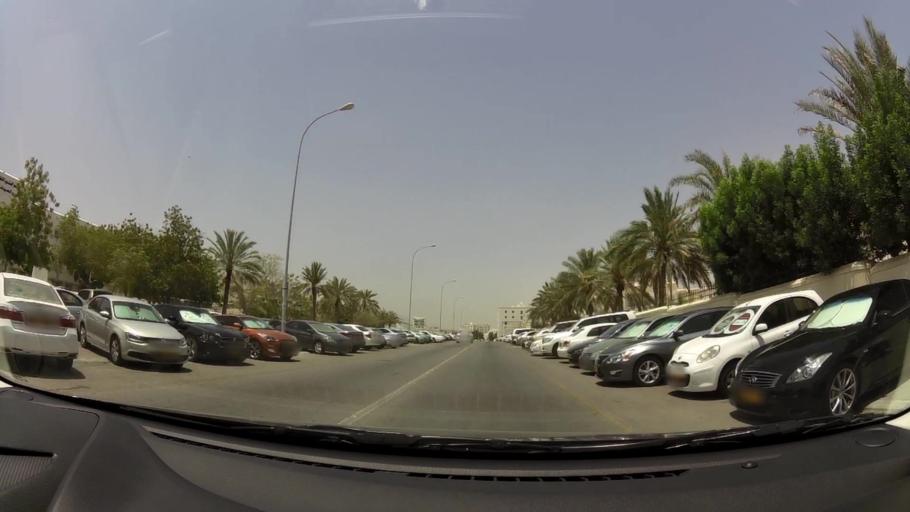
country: OM
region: Muhafazat Masqat
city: Bawshar
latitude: 23.5792
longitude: 58.4300
